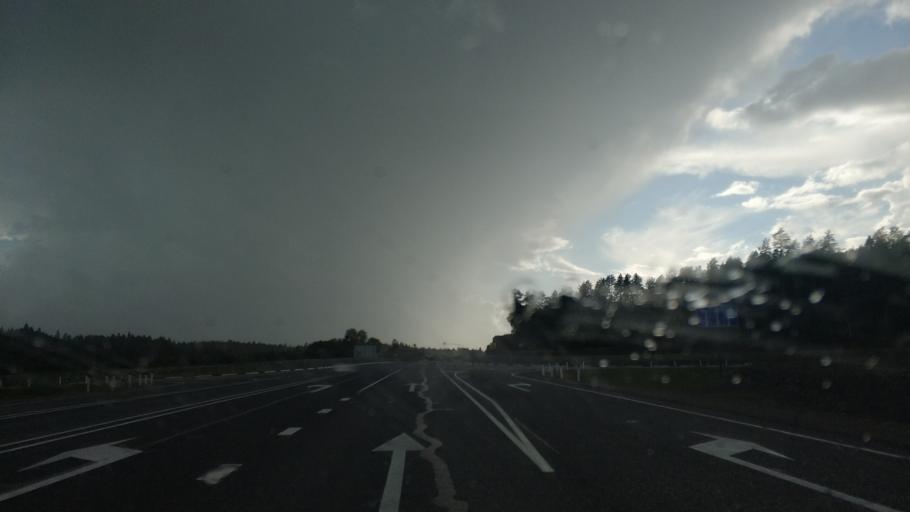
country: RU
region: Leningrad
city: Kuznechnoye
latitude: 61.3396
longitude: 29.8605
